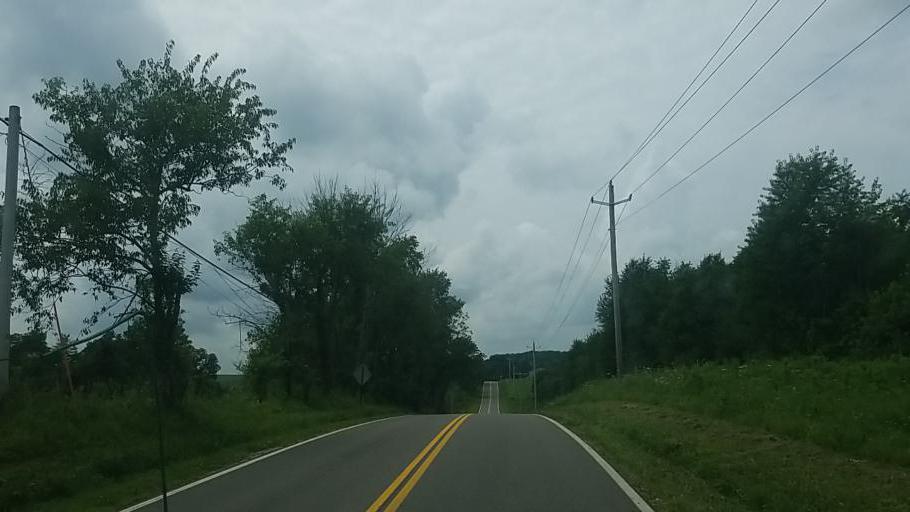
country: US
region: Ohio
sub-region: Licking County
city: Utica
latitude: 40.2041
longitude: -82.3692
